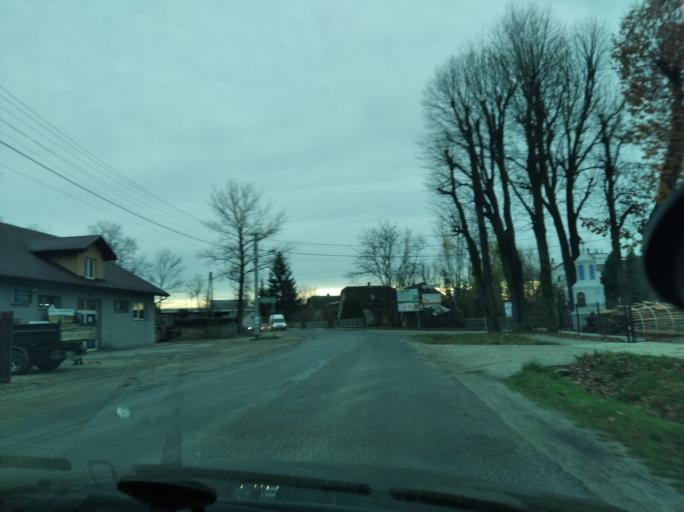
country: PL
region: Subcarpathian Voivodeship
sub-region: Powiat lancucki
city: Czarna
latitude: 50.0925
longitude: 22.1842
